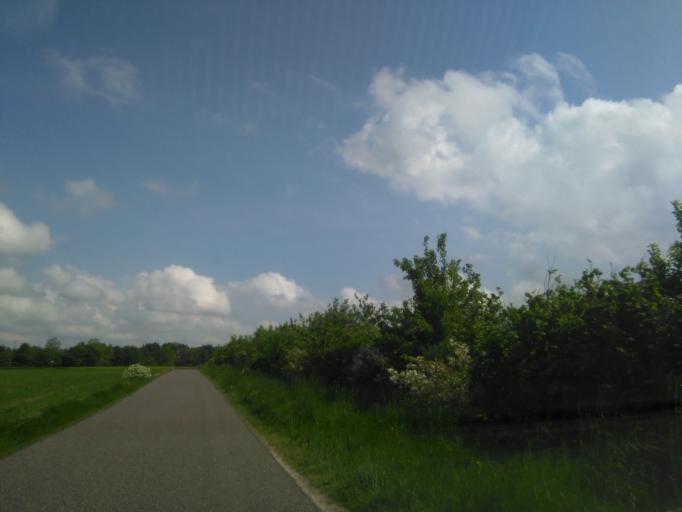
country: DK
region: Central Jutland
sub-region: Skanderborg Kommune
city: Skovby
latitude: 56.2062
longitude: 9.9483
